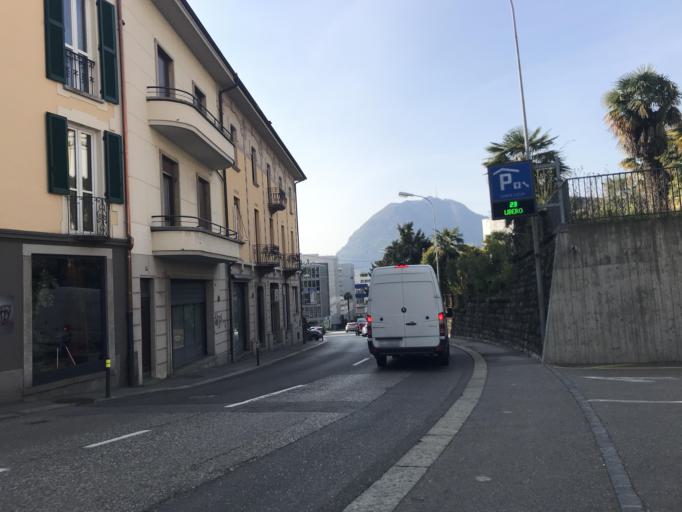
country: CH
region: Ticino
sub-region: Lugano District
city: Massagno
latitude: 46.0106
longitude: 8.9465
